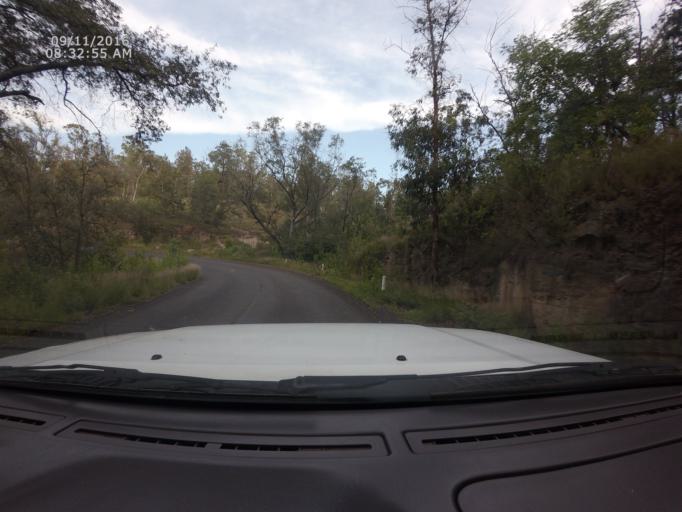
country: MX
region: Michoacan
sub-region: Morelia
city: Morelos
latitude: 19.6308
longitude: -101.2509
